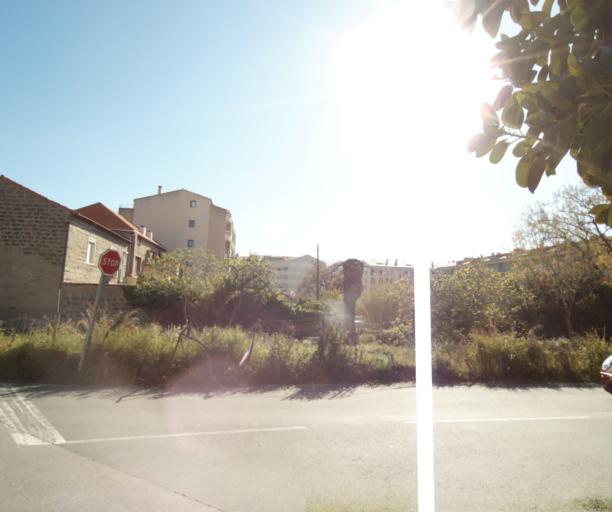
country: FR
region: Corsica
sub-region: Departement de la Corse-du-Sud
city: Propriano
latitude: 41.6750
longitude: 8.8987
